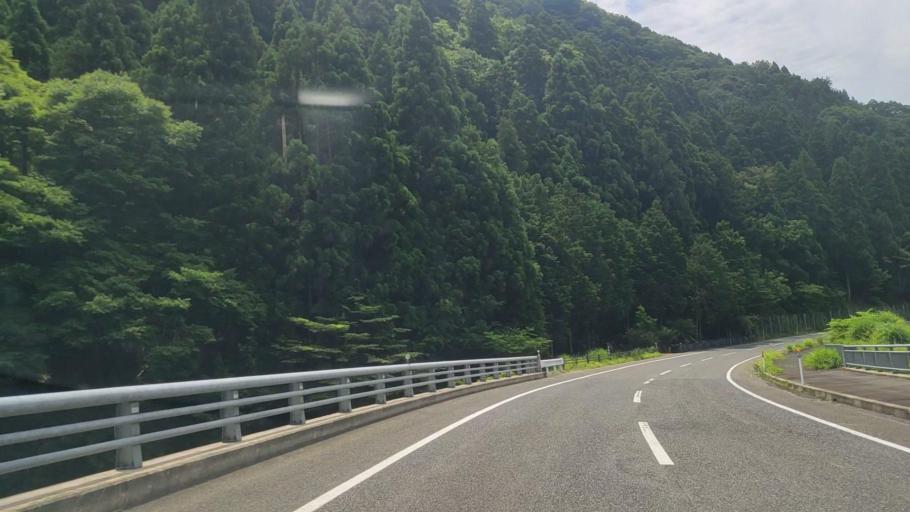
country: JP
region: Hyogo
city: Toyooka
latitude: 35.4917
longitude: 134.5615
